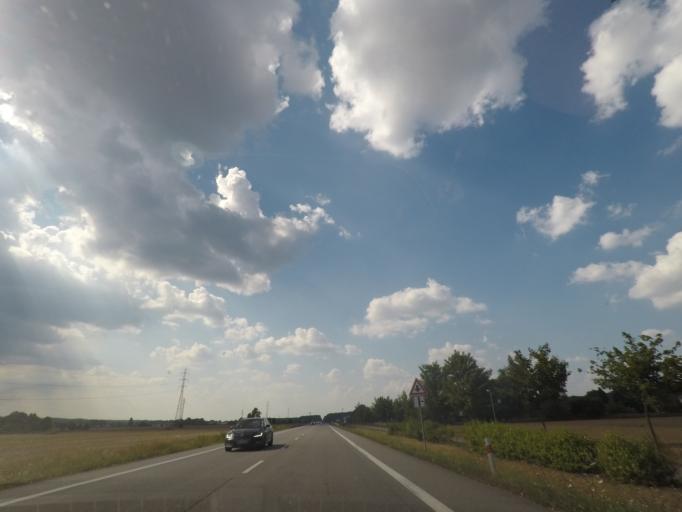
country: CZ
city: Albrechtice nad Orlici
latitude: 50.1660
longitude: 16.0484
